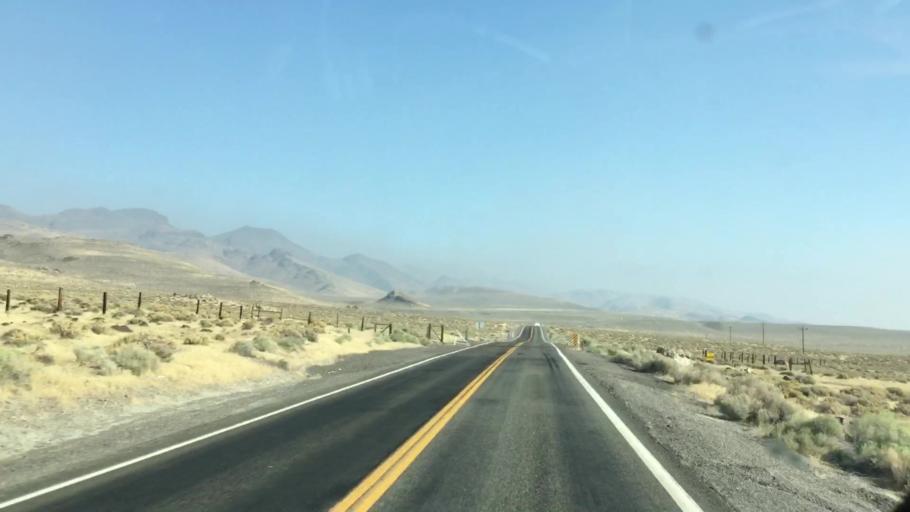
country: US
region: Nevada
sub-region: Lyon County
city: Fernley
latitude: 39.9886
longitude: -119.3859
